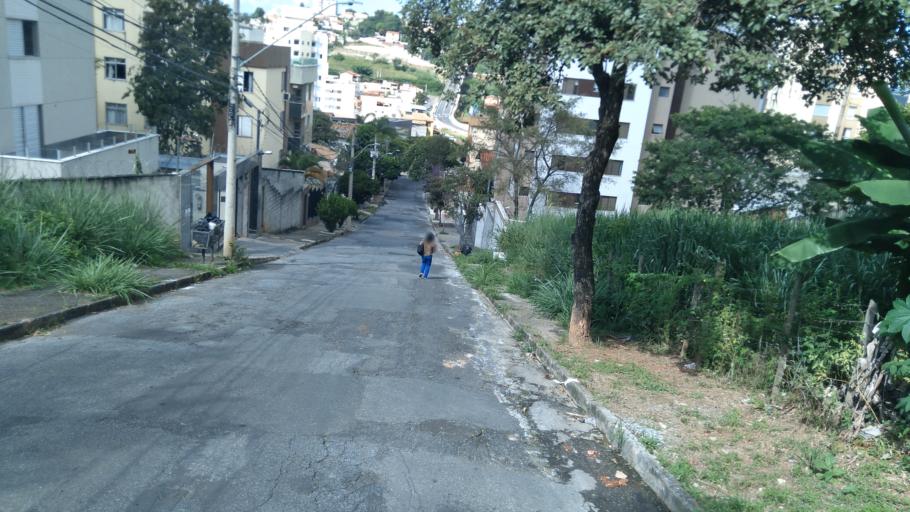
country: BR
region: Minas Gerais
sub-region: Belo Horizonte
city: Belo Horizonte
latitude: -19.8729
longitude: -43.9166
